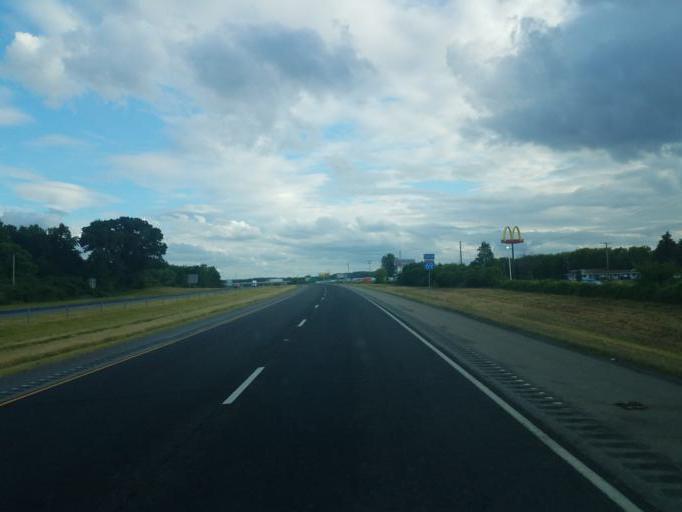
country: US
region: Indiana
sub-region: Steuben County
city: Fremont
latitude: 41.7412
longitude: -84.9994
